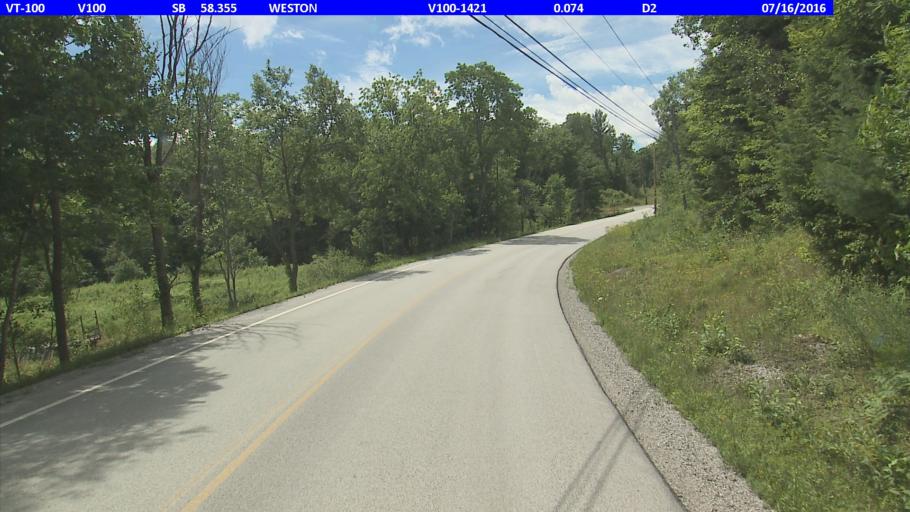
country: US
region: Vermont
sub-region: Windsor County
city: Chester
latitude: 43.2507
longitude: -72.7950
